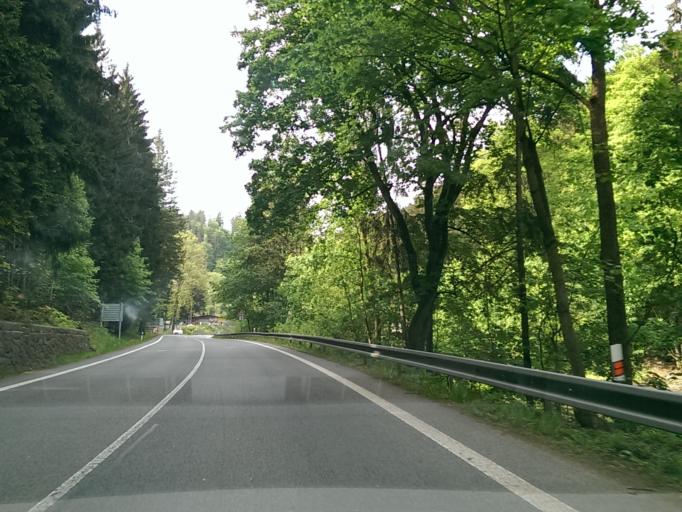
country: CZ
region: Liberecky
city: Zelezny Brod
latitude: 50.6510
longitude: 15.2558
